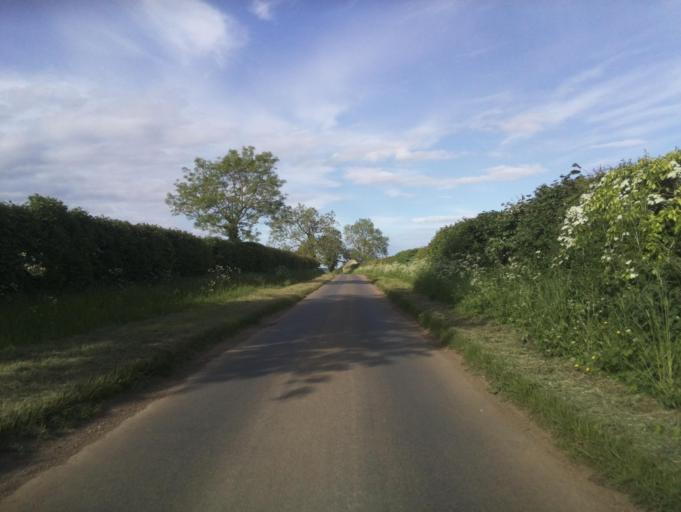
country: GB
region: England
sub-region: Gloucestershire
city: Westfield
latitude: 51.9254
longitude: -1.8395
